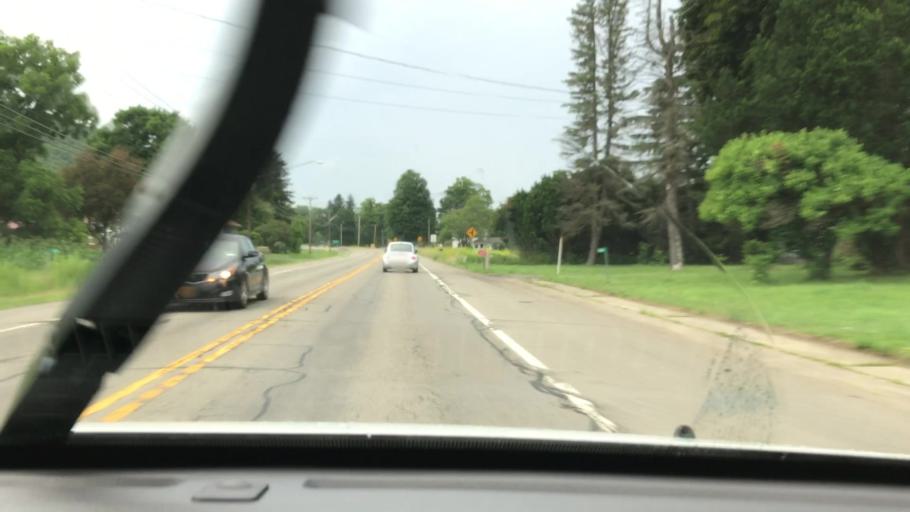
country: US
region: New York
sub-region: Cattaraugus County
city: Salamanca
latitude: 42.2199
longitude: -78.6370
